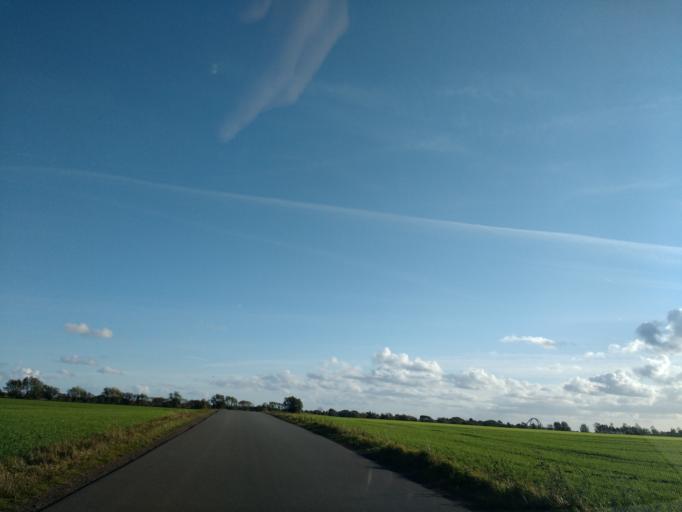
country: DE
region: Schleswig-Holstein
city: Grossenbrode
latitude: 54.4301
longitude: 11.1169
